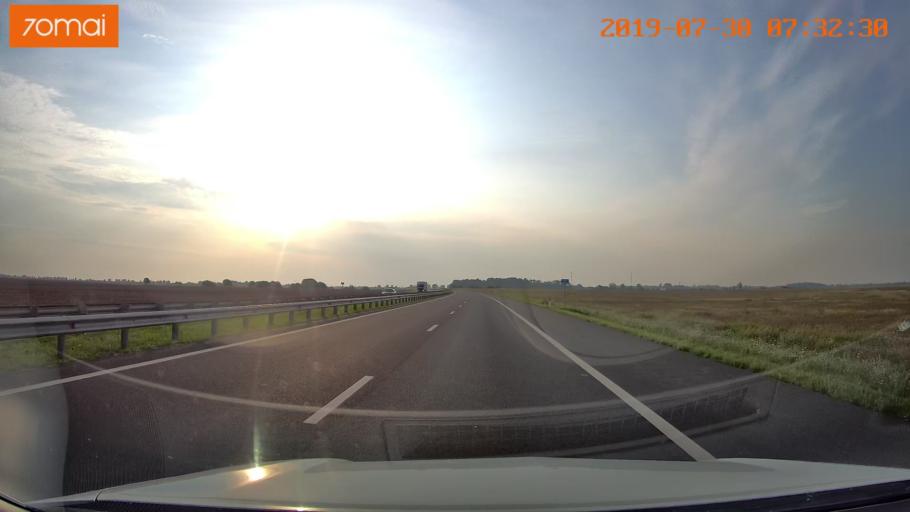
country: RU
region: Kaliningrad
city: Gvardeysk
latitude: 54.6673
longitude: 21.0210
